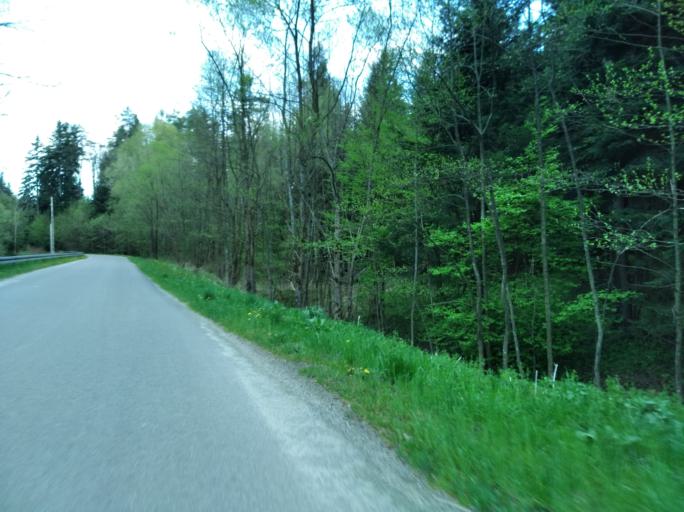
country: PL
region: Subcarpathian Voivodeship
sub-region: Powiat strzyzowski
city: Strzyzow
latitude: 49.8078
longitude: 21.8254
